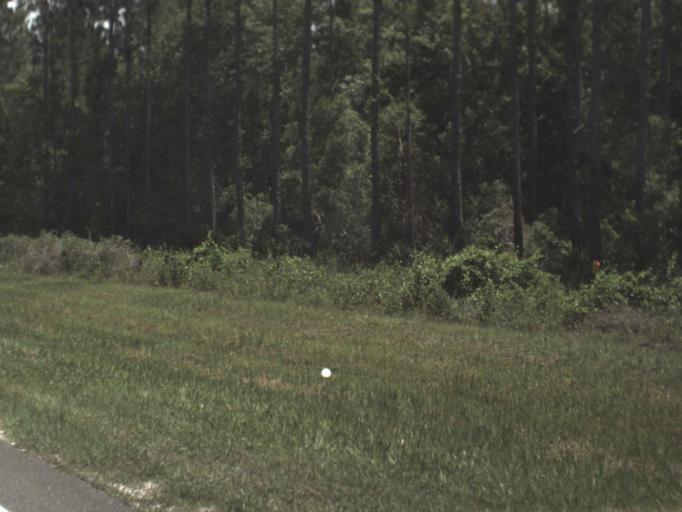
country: US
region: Florida
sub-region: Clay County
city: Keystone Heights
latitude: 29.7414
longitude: -82.0514
